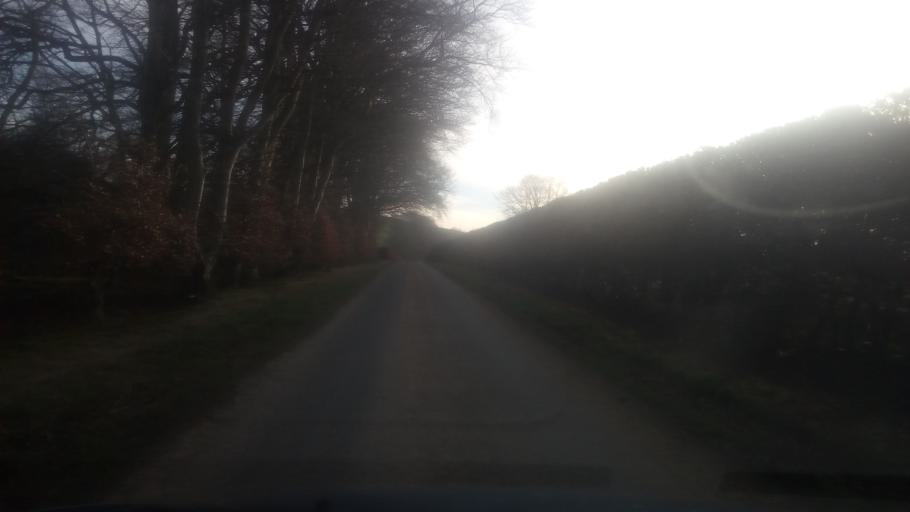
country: GB
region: Scotland
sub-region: The Scottish Borders
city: Jedburgh
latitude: 55.4688
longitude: -2.6279
